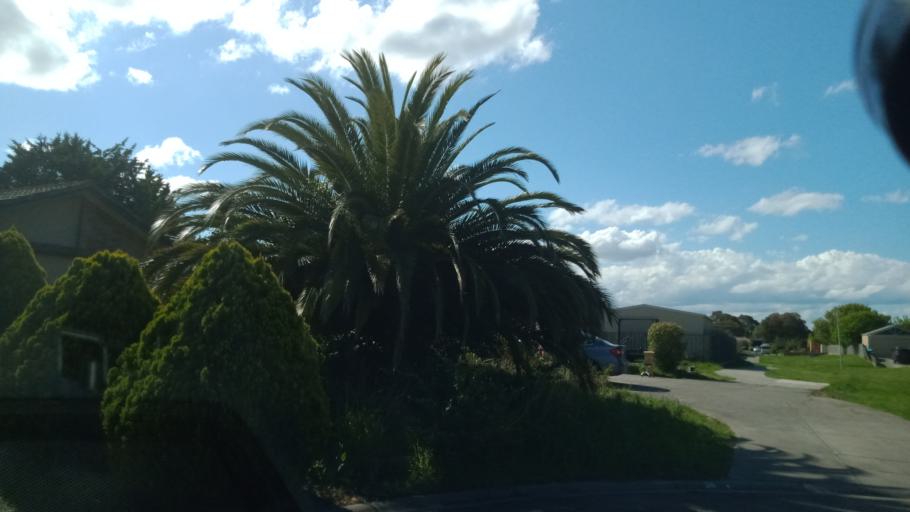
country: AU
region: Victoria
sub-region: Casey
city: Cranbourne West
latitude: -38.1014
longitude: 145.2564
